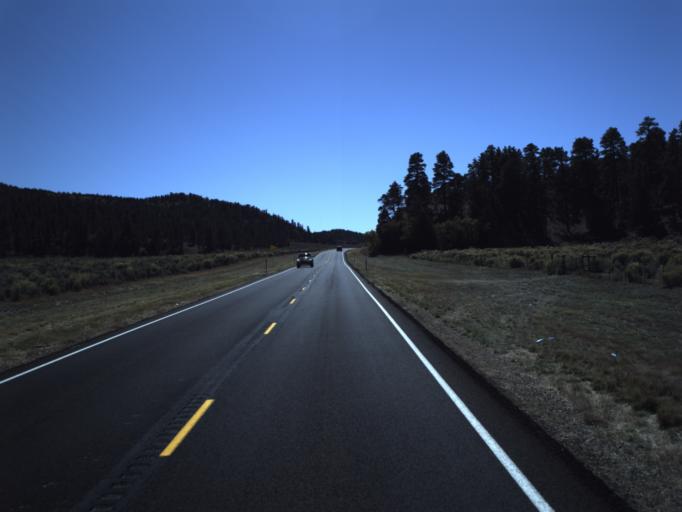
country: US
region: Utah
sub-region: Garfield County
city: Panguitch
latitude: 37.6643
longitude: -111.8322
